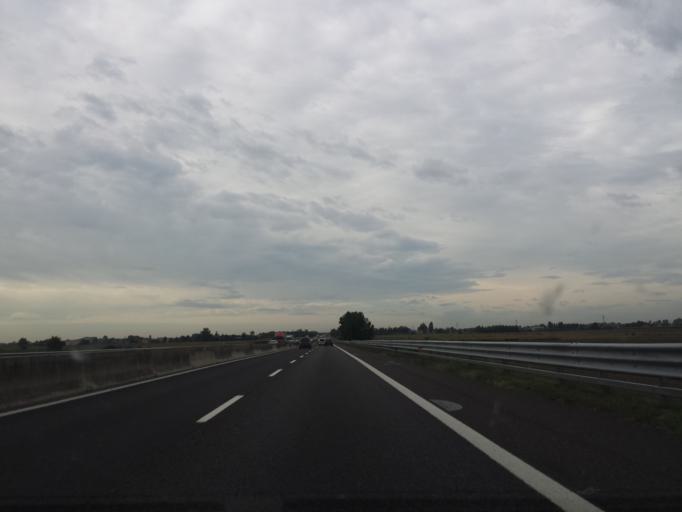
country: IT
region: Veneto
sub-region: Provincia di Padova
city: Solesino
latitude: 45.1674
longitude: 11.7759
